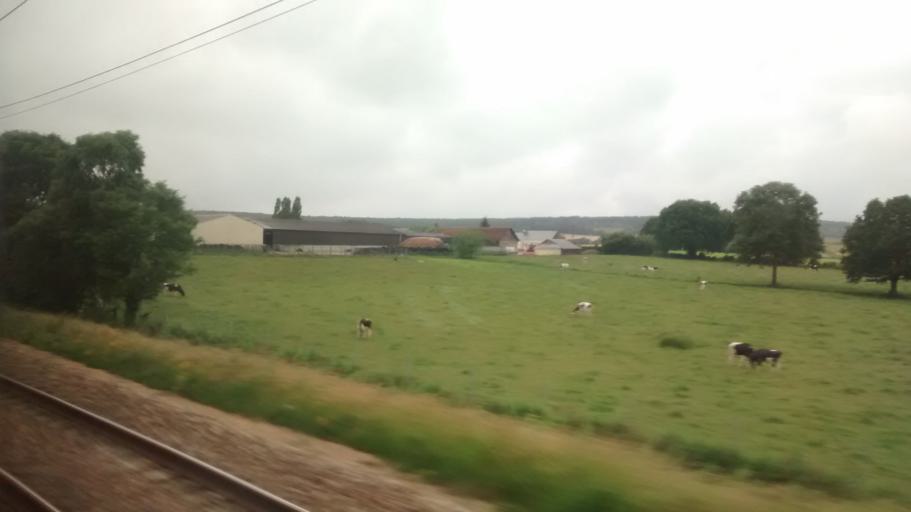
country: FR
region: Pays de la Loire
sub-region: Departement de la Sarthe
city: Vibraye
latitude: 48.0853
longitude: 0.8515
